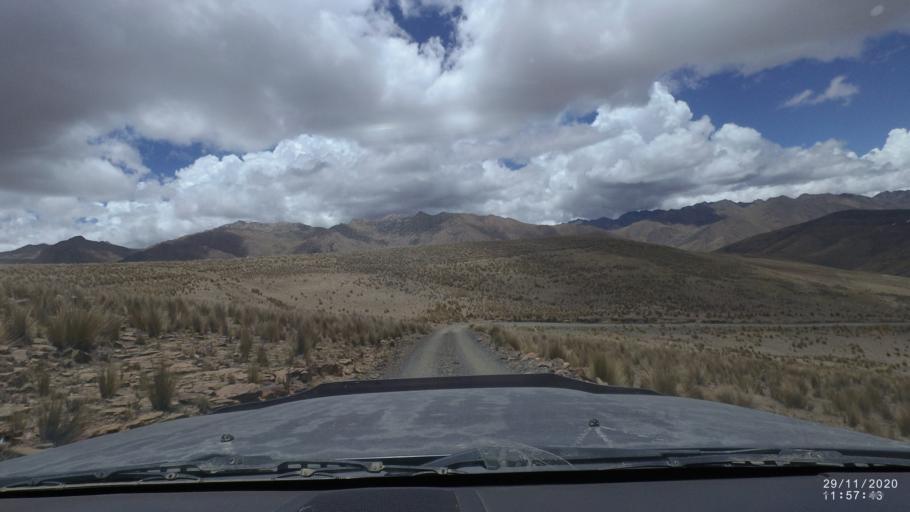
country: BO
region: Cochabamba
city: Cochabamba
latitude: -17.1577
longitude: -66.2740
